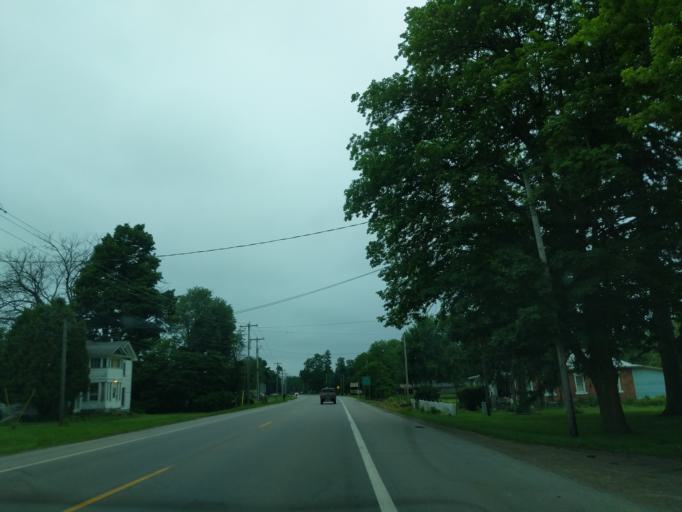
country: US
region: Michigan
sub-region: Branch County
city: Quincy
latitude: 41.9481
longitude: -84.8685
